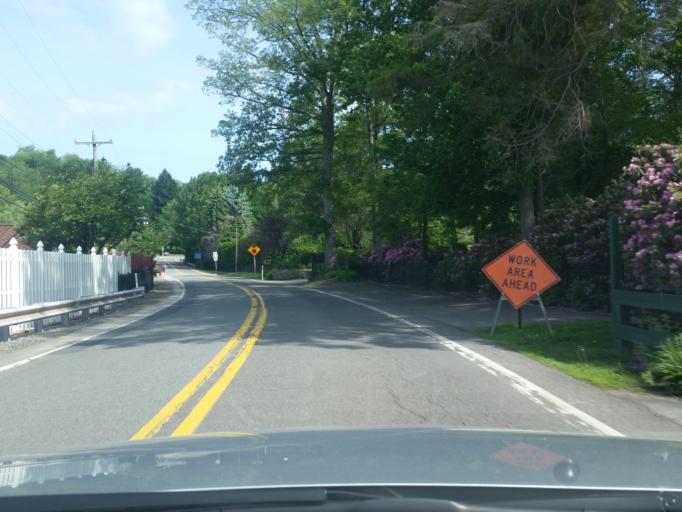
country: US
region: Pennsylvania
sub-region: Luzerne County
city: Harveys Lake
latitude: 41.3796
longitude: -76.0255
